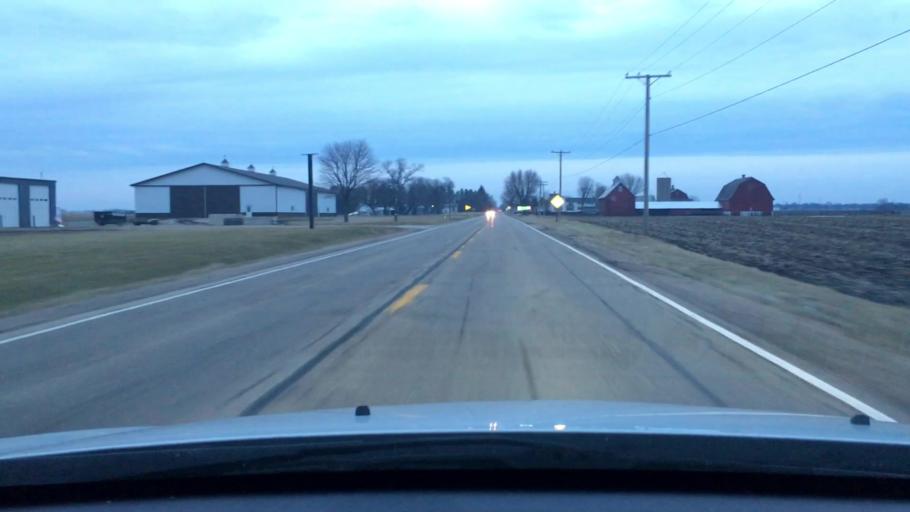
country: US
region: Illinois
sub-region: LaSalle County
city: Mendota
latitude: 41.5135
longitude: -89.1272
